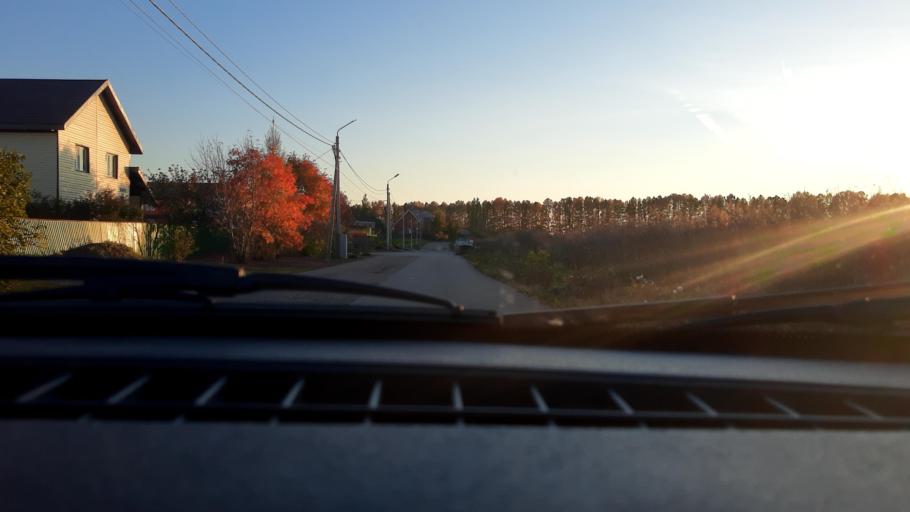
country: RU
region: Bashkortostan
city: Ufa
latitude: 54.8570
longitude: 56.0132
